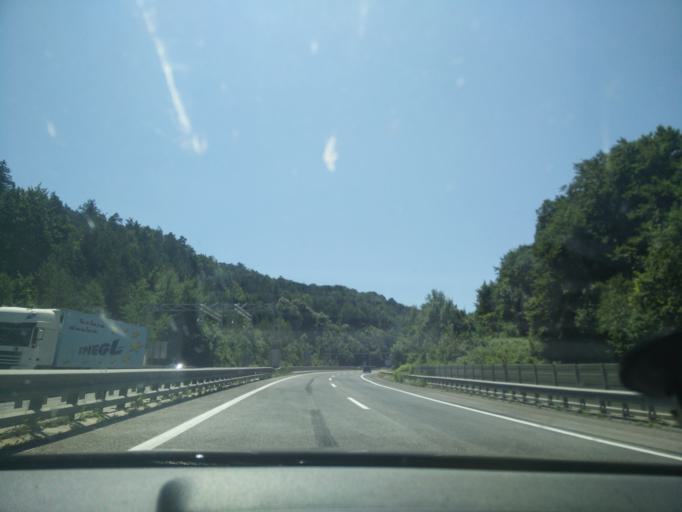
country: AT
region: Lower Austria
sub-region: Politischer Bezirk Neunkirchen
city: Grimmenstein
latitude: 47.6253
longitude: 16.1321
